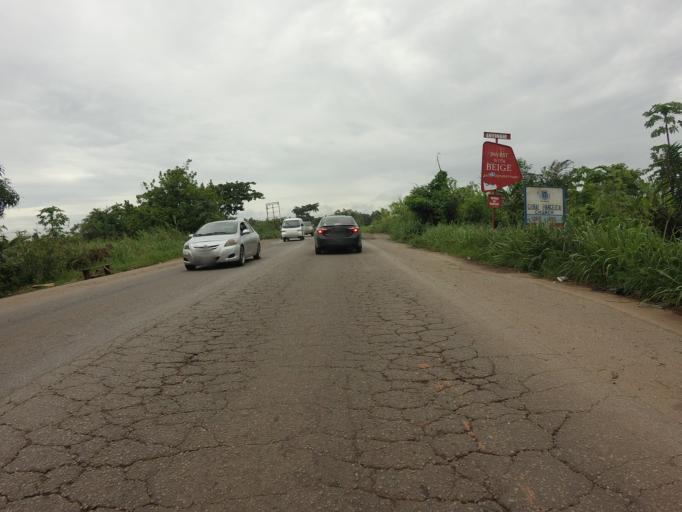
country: GH
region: Eastern
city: Begoro
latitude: 6.3870
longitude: -0.5533
